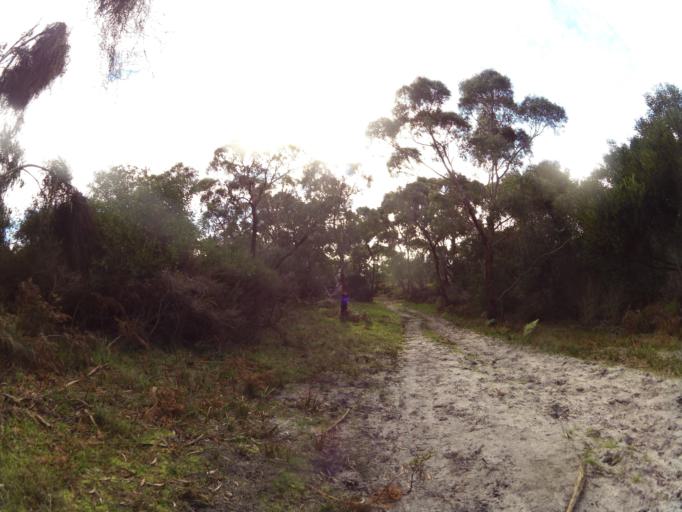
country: AU
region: Victoria
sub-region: Bass Coast
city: North Wonthaggi
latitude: -38.6273
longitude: 145.5734
